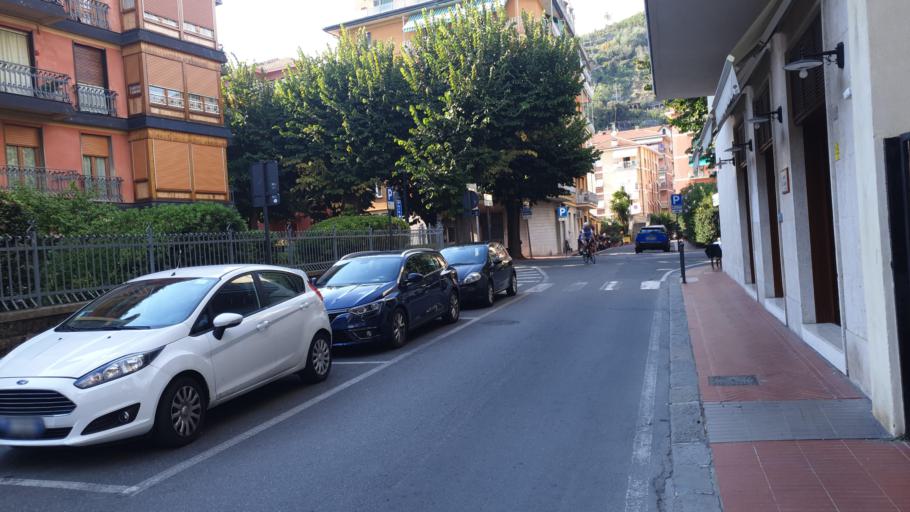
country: IT
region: Liguria
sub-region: Provincia di La Spezia
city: Levanto
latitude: 44.1709
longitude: 9.6109
